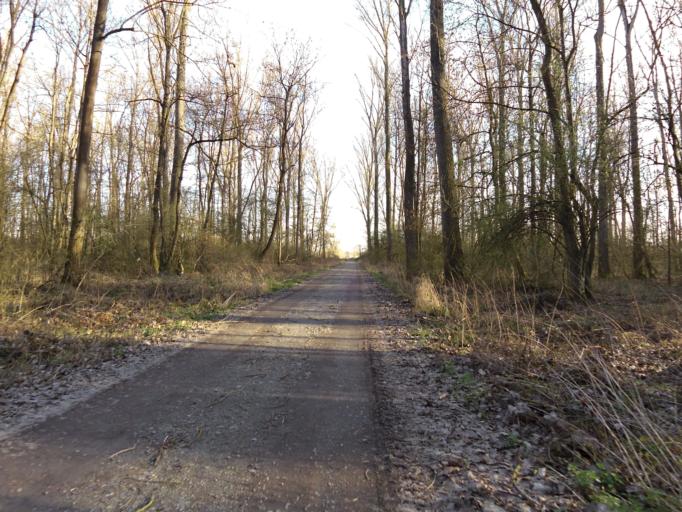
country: DE
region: Hesse
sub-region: Regierungsbezirk Darmstadt
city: Biblis
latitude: 49.6765
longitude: 8.4416
